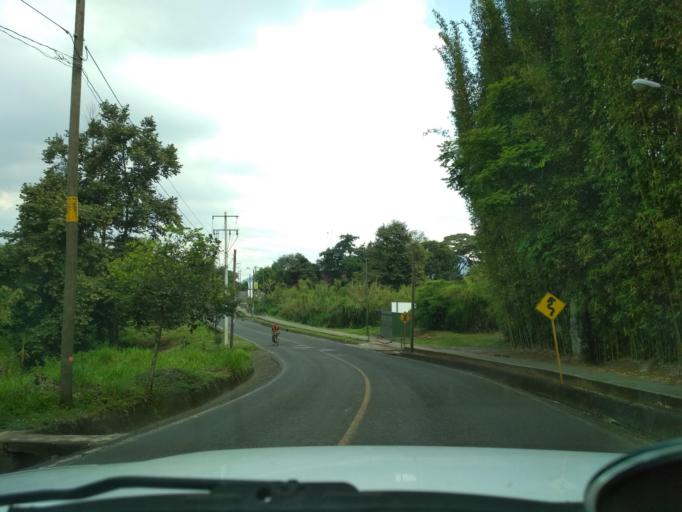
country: MX
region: Veracruz
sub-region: Ixtaczoquitlan
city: Buenavista
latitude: 18.9137
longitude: -97.0264
